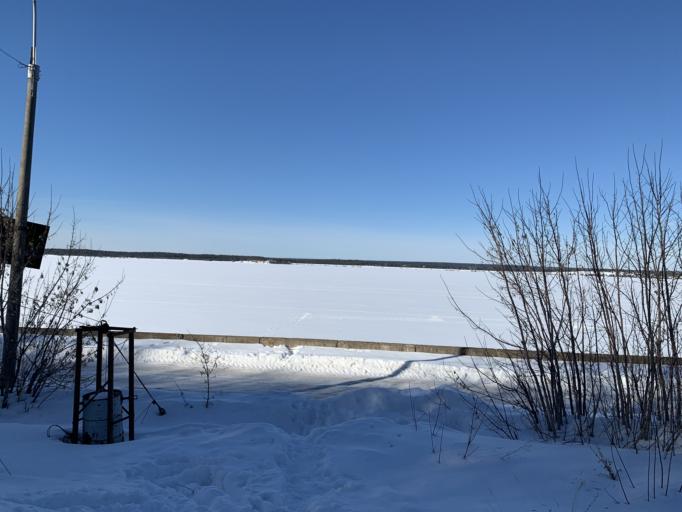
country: RU
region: Chuvashia
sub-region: Cheboksarskiy Rayon
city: Cheboksary
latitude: 56.1502
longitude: 47.2714
